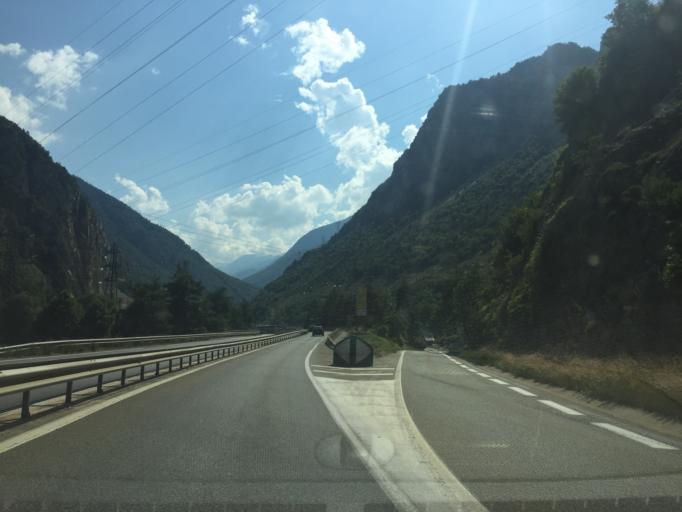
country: FR
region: Rhone-Alpes
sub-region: Departement de la Savoie
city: Moutiers
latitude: 45.4965
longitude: 6.5550
